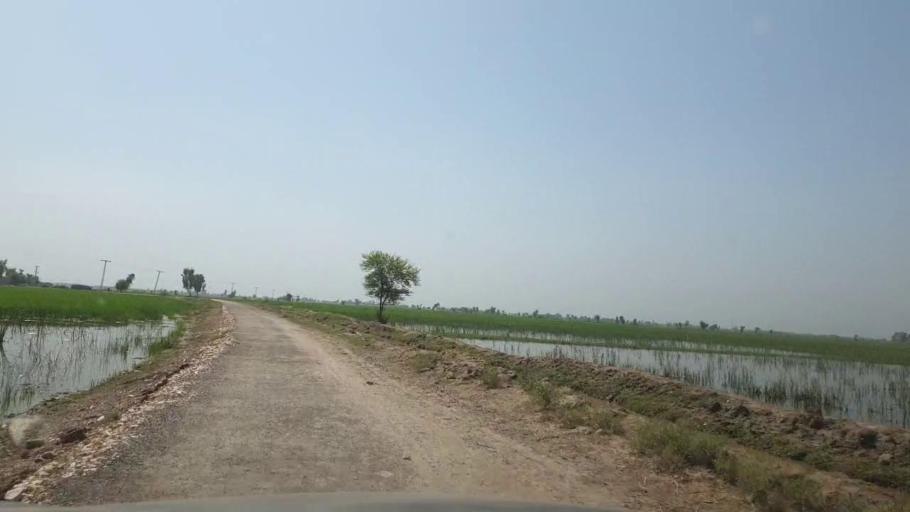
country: PK
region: Sindh
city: Warah
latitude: 27.4863
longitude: 67.7788
